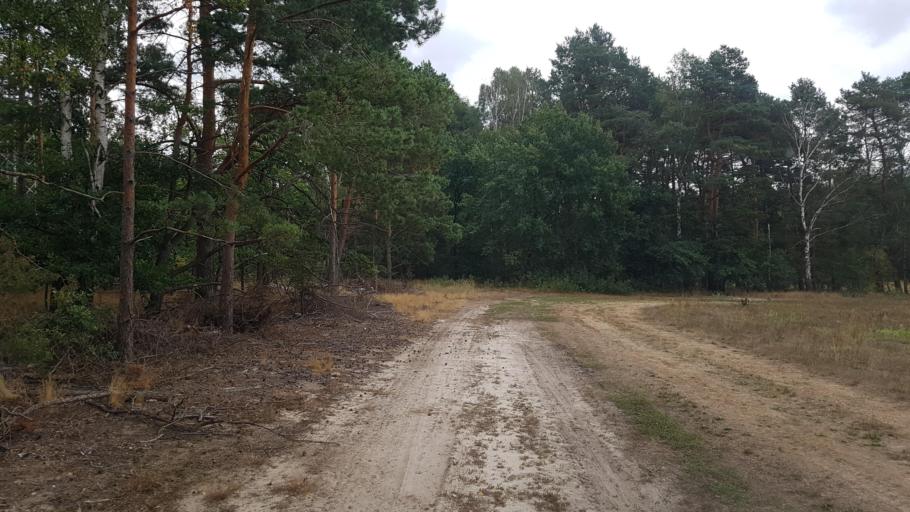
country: DE
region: Brandenburg
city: Sallgast
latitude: 51.6237
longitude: 13.8370
